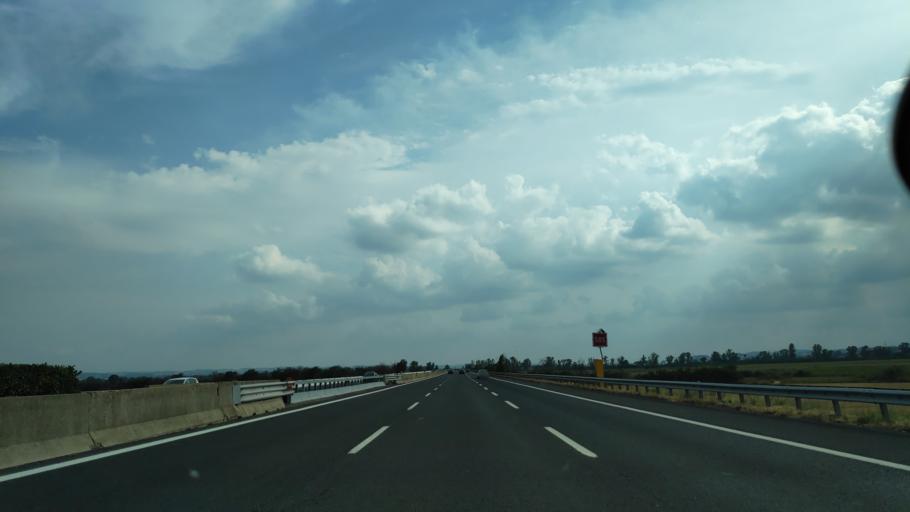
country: IT
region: Latium
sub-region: Citta metropolitana di Roma Capitale
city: Fiano Romano
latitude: 42.1427
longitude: 12.6216
